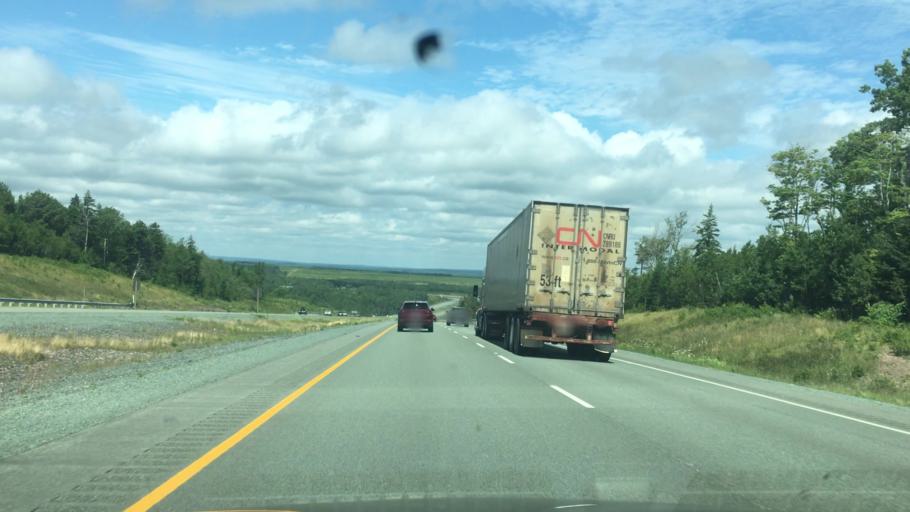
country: CA
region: Nova Scotia
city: Oxford
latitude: 45.5950
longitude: -63.7270
